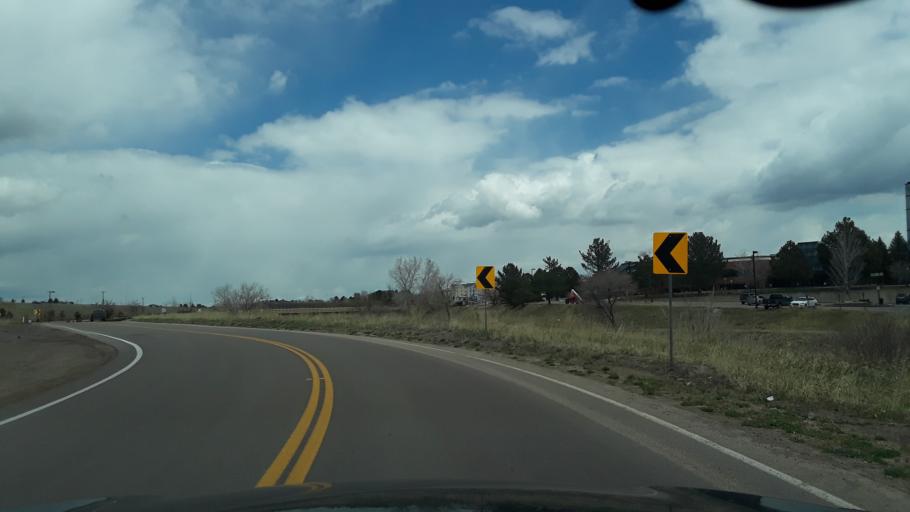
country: US
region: Colorado
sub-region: El Paso County
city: Air Force Academy
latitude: 38.9285
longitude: -104.8156
